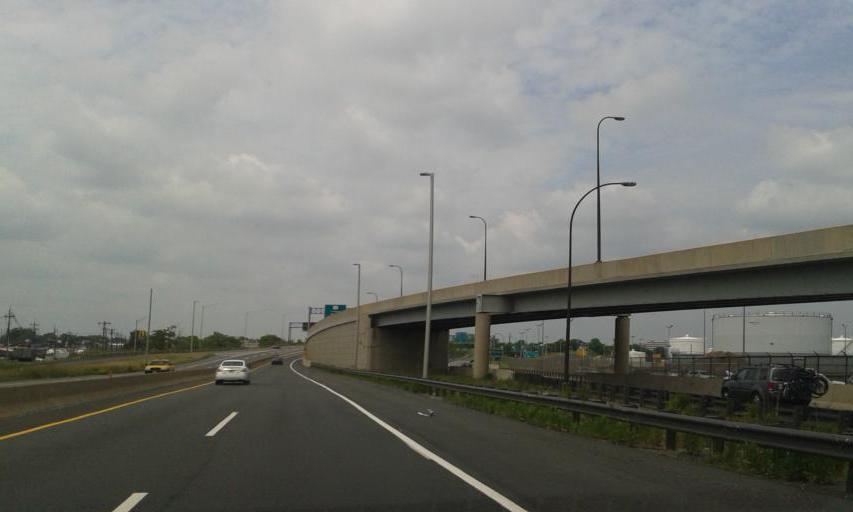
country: US
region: New Jersey
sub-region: Union County
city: Elizabeth
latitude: 40.6737
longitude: -74.1874
